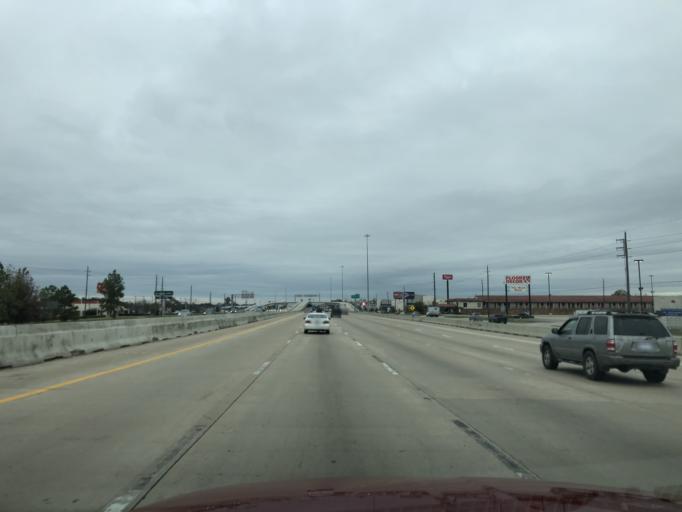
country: US
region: Texas
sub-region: Harris County
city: Spring
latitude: 30.0180
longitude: -95.4287
